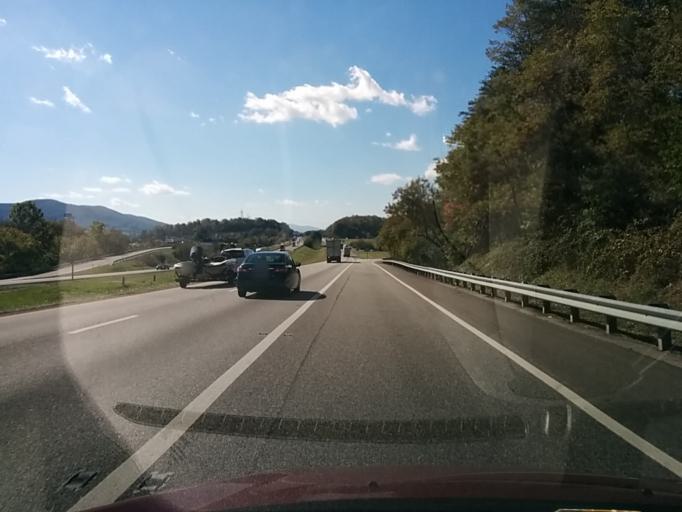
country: US
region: Virginia
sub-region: Botetourt County
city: Daleville
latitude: 37.3940
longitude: -79.9021
